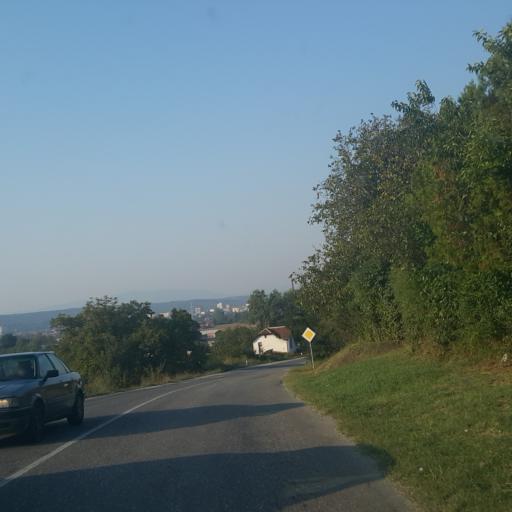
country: RS
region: Central Serbia
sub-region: Zajecarski Okrug
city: Zajecar
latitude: 43.9204
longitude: 22.2921
